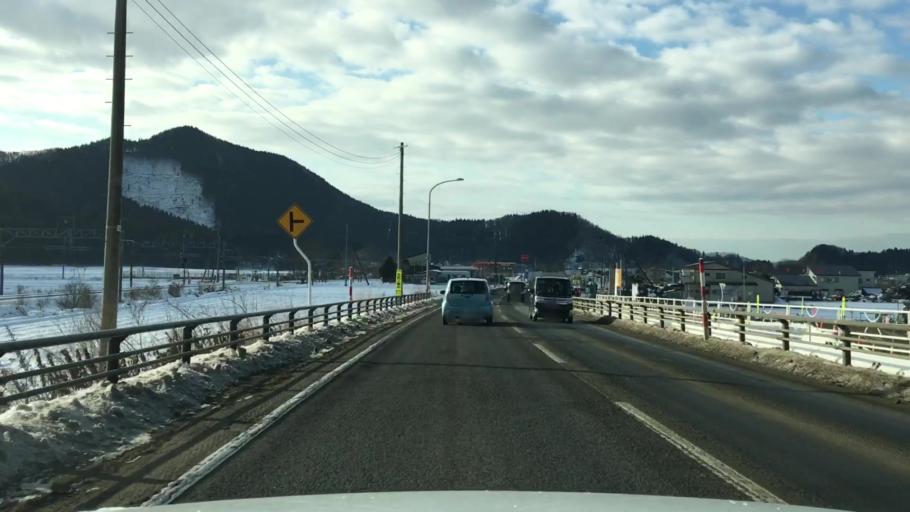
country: JP
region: Akita
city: Odate
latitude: 40.3434
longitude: 140.5967
